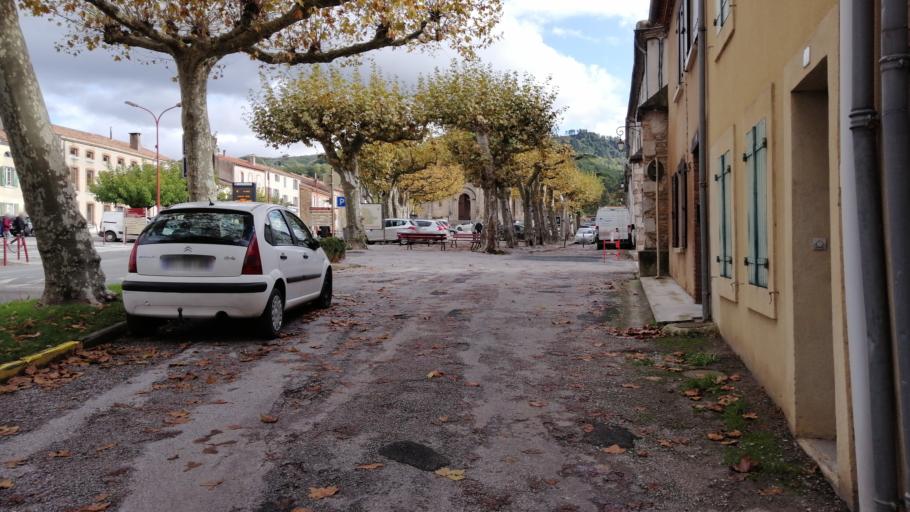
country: FR
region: Midi-Pyrenees
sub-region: Departement du Tarn
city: Soreze
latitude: 43.4539
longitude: 2.0676
